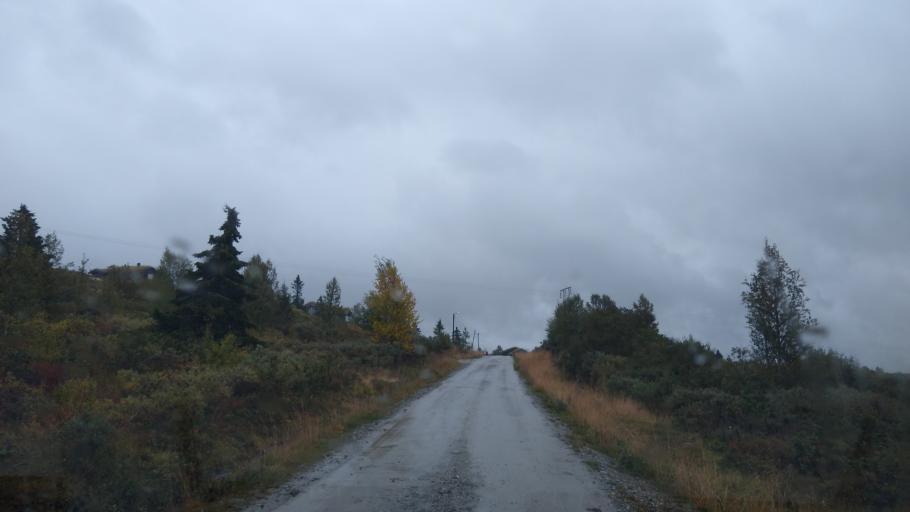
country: NO
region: Oppland
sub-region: Ringebu
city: Ringebu
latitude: 61.6728
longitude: 10.0926
